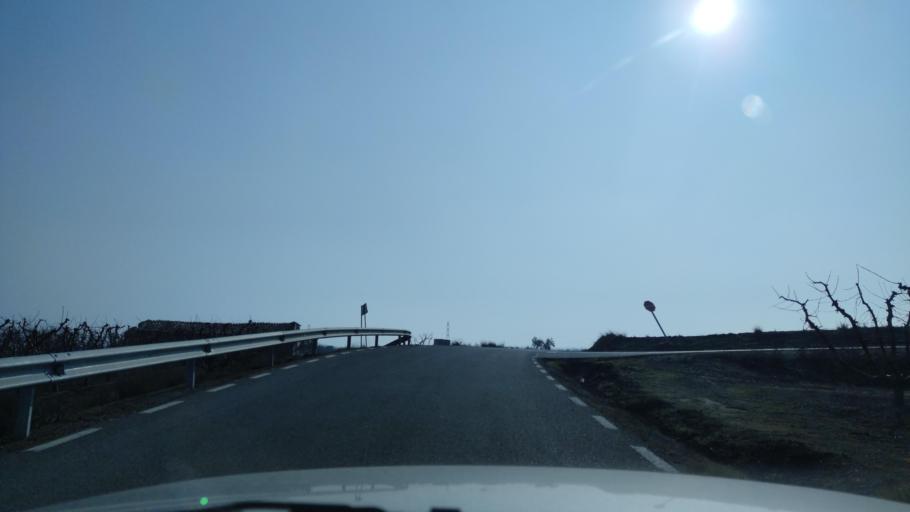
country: ES
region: Catalonia
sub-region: Provincia de Lleida
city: Sunyer
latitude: 41.5551
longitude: 0.5728
